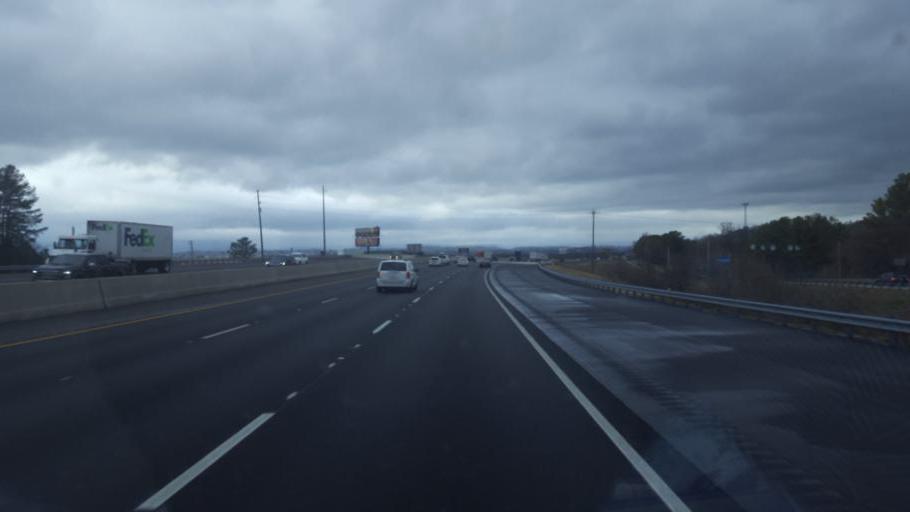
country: US
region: Georgia
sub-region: Catoosa County
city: Indian Springs
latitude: 34.9666
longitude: -85.1894
